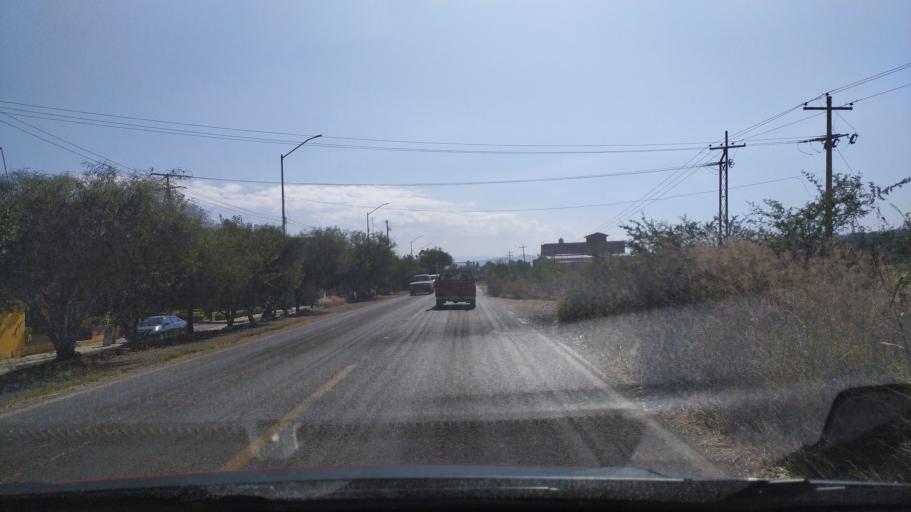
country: MX
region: Guanajuato
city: Ciudad Manuel Doblado
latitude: 20.7432
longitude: -101.9574
